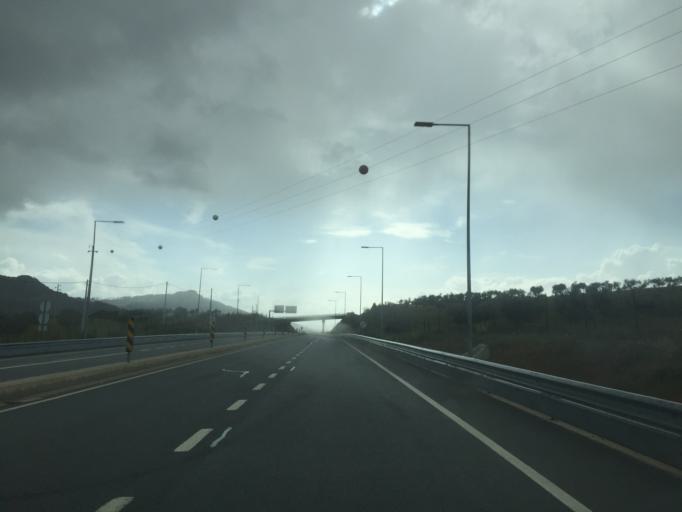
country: PT
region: Braganca
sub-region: Mogadouro
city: Mogadouro
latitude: 41.3399
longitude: -6.6914
